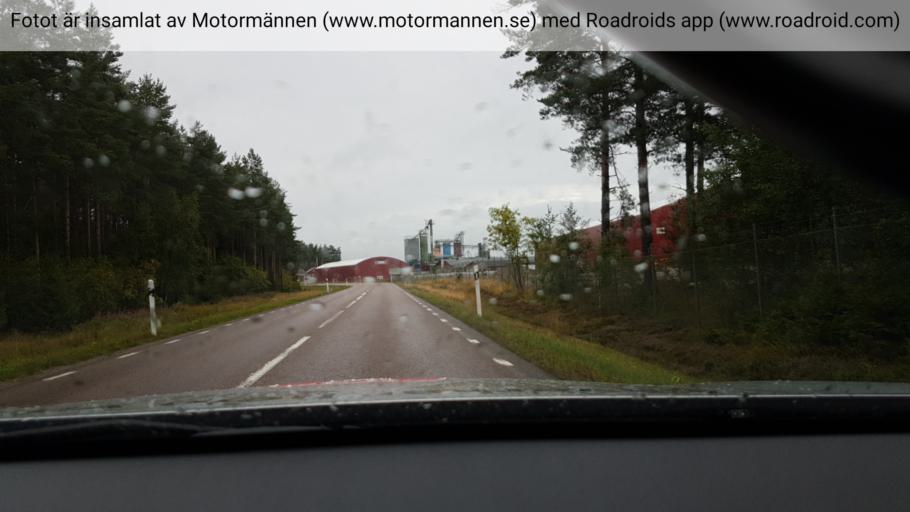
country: SE
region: Gaevleborg
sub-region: Gavle Kommun
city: Hedesunda
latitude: 60.5335
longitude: 16.9447
